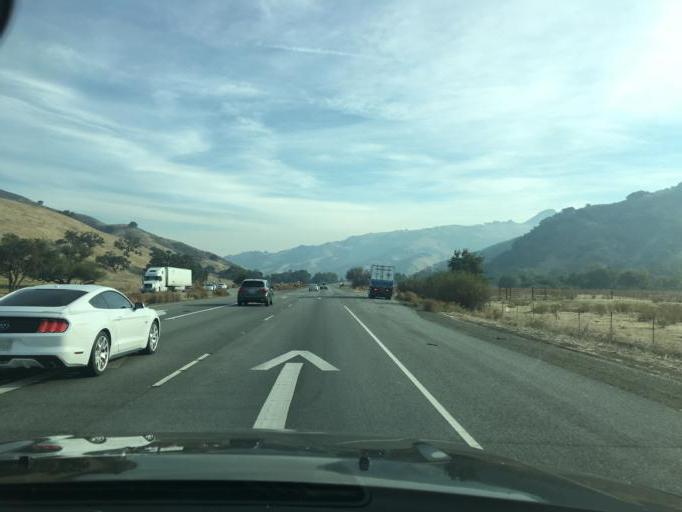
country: US
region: California
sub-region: San Benito County
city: Hollister
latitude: 37.0098
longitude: -121.3566
